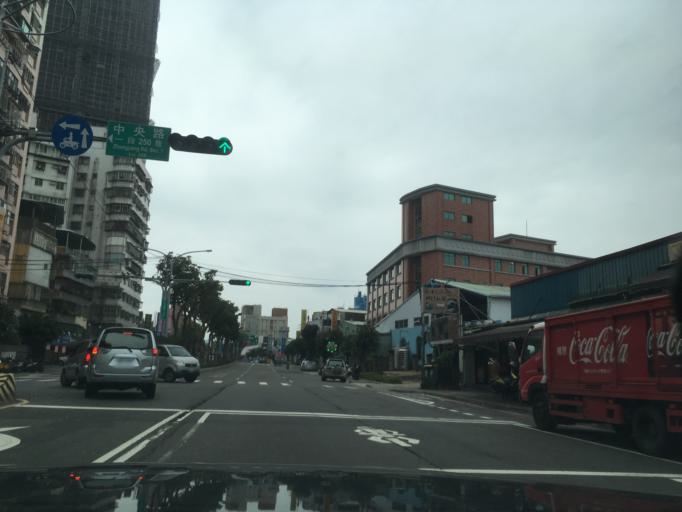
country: TW
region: Taipei
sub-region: Taipei
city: Banqiao
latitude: 24.9855
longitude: 121.4432
